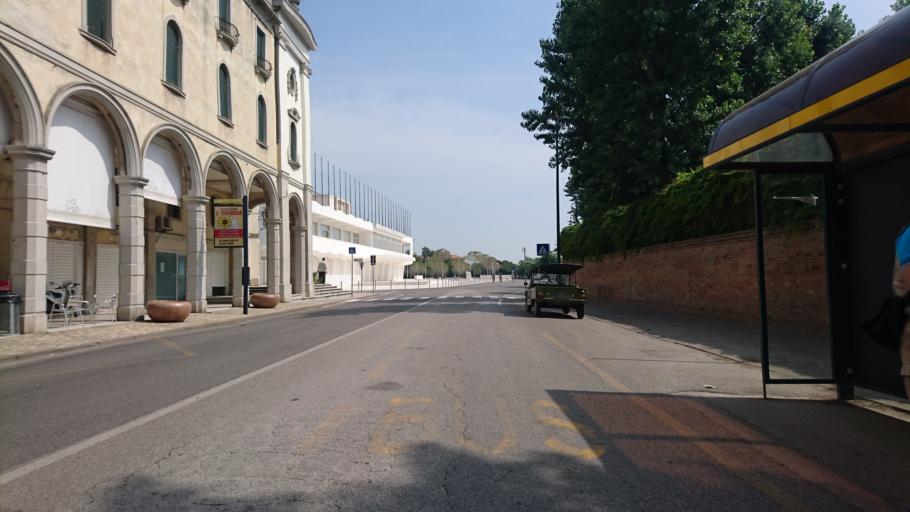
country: IT
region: Veneto
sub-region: Provincia di Venezia
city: Lido
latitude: 45.4048
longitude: 12.3669
